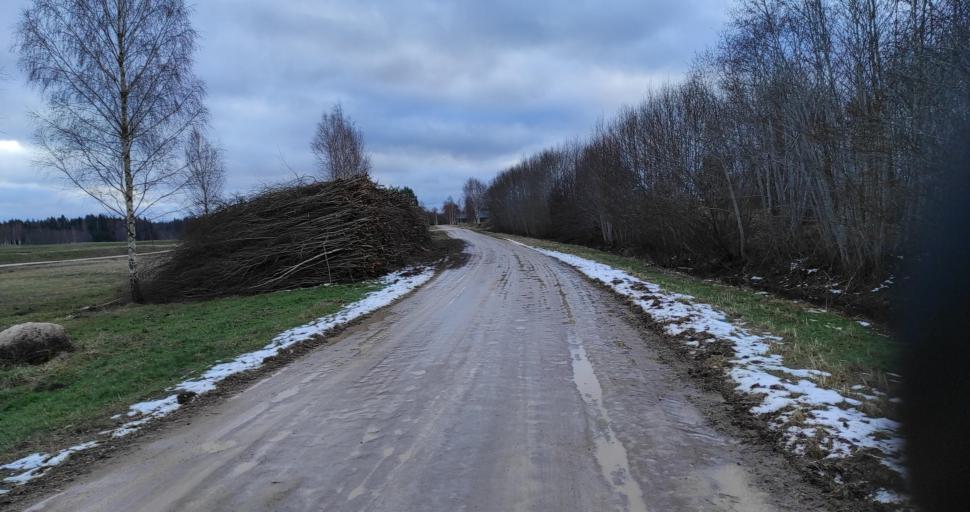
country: LV
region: Talsu Rajons
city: Stende
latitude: 57.0644
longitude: 22.2893
